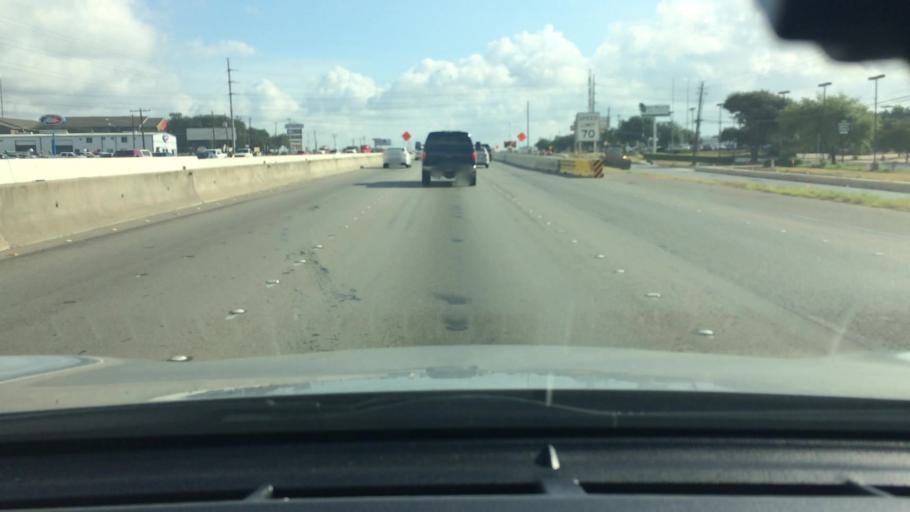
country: US
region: Texas
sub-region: Travis County
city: Onion Creek
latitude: 30.1851
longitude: -97.7739
